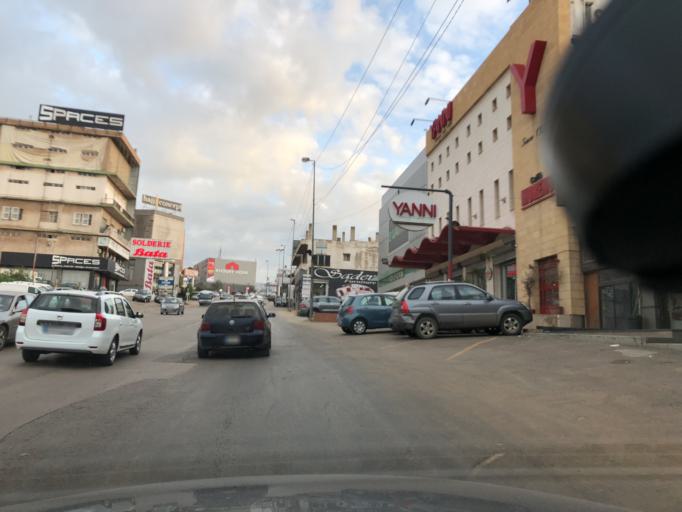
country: LB
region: Mont-Liban
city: Baabda
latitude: 33.8651
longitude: 35.5462
